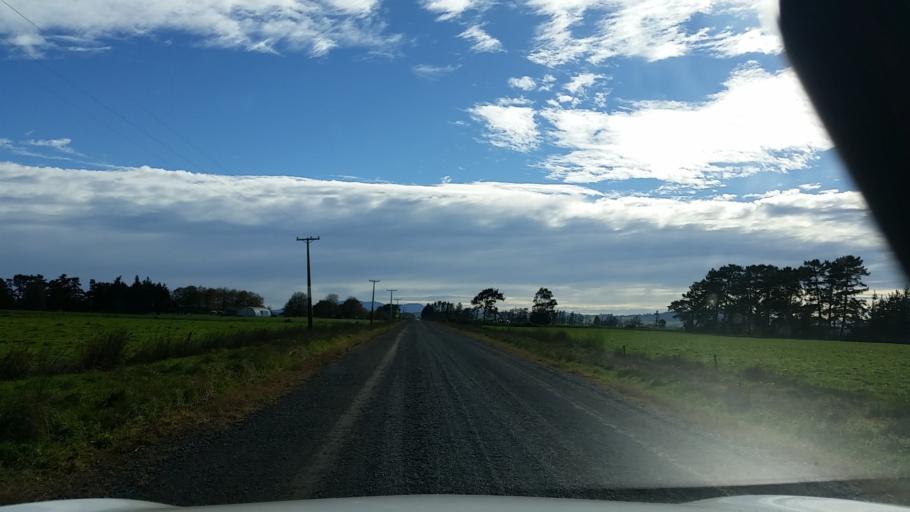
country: NZ
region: Waikato
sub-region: Hamilton City
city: Hamilton
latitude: -37.6676
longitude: 175.4394
